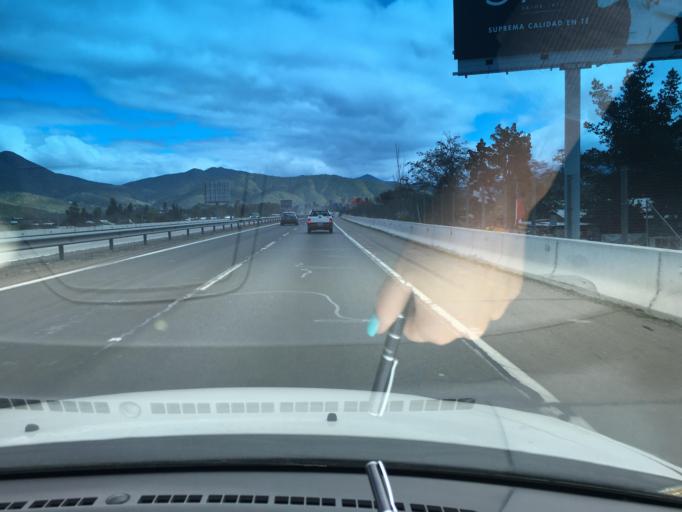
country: CL
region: Santiago Metropolitan
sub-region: Provincia de Melipilla
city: Melipilla
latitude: -33.4108
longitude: -71.1426
